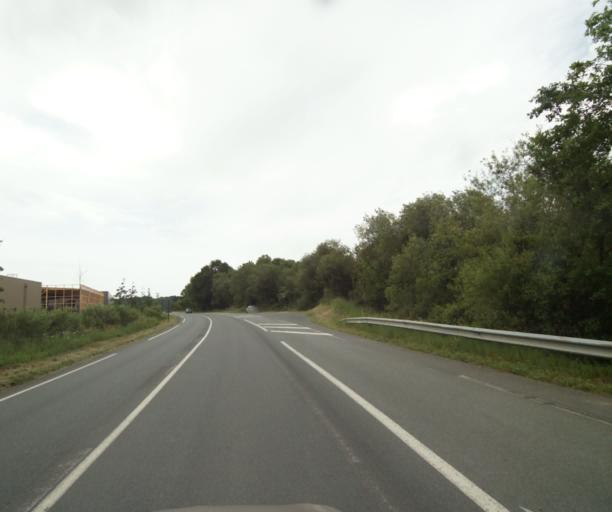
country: FR
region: Aquitaine
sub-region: Departement des Pyrenees-Atlantiques
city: Mouguerre
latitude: 43.4927
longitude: -1.4251
